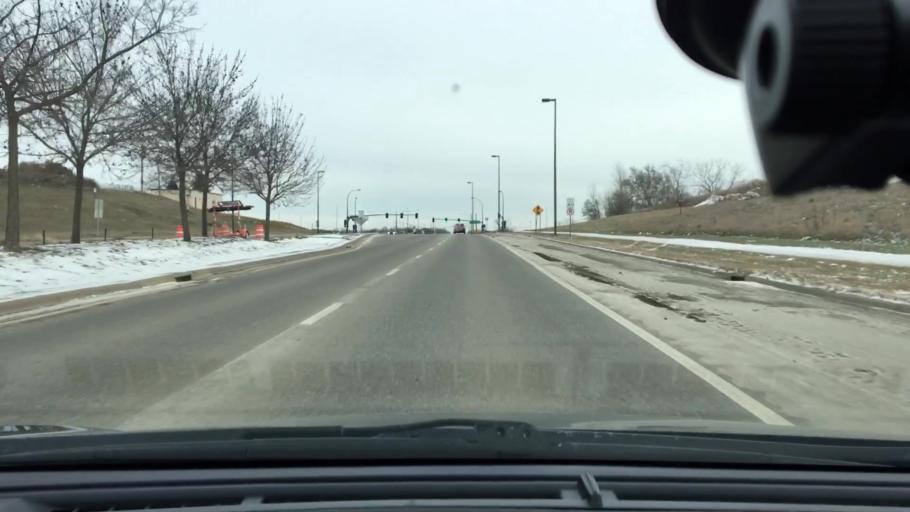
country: US
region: Minnesota
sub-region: Hennepin County
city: Osseo
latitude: 45.0945
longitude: -93.4086
